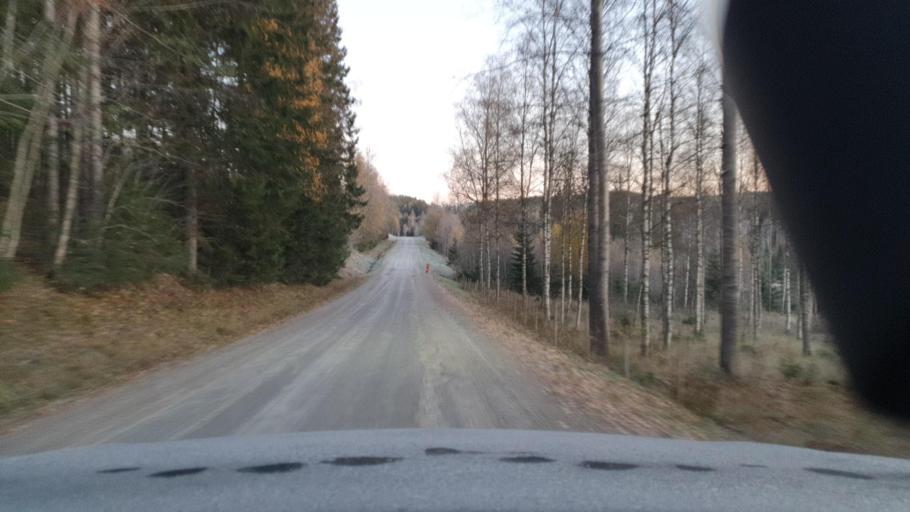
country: SE
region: Vaermland
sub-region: Arvika Kommun
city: Arvika
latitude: 59.8312
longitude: 12.7476
